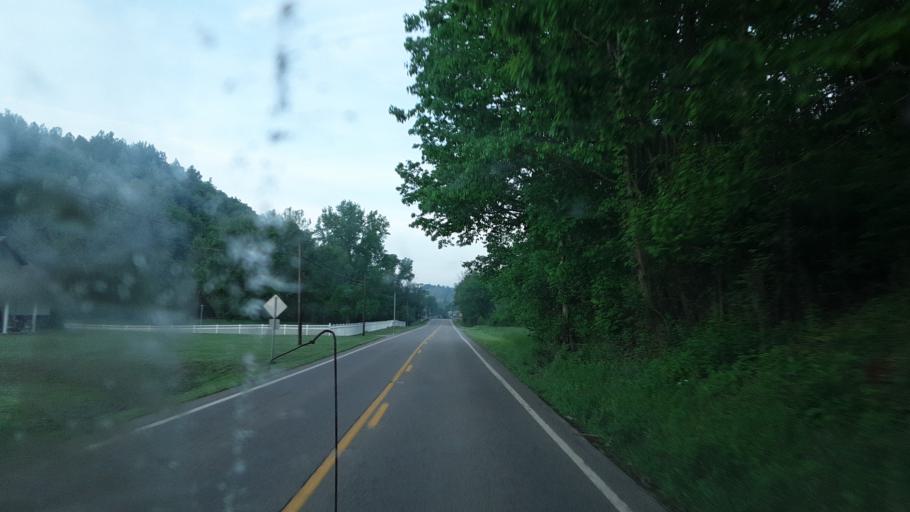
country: US
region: Ohio
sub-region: Ross County
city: Kingston
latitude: 39.4810
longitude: -82.7357
